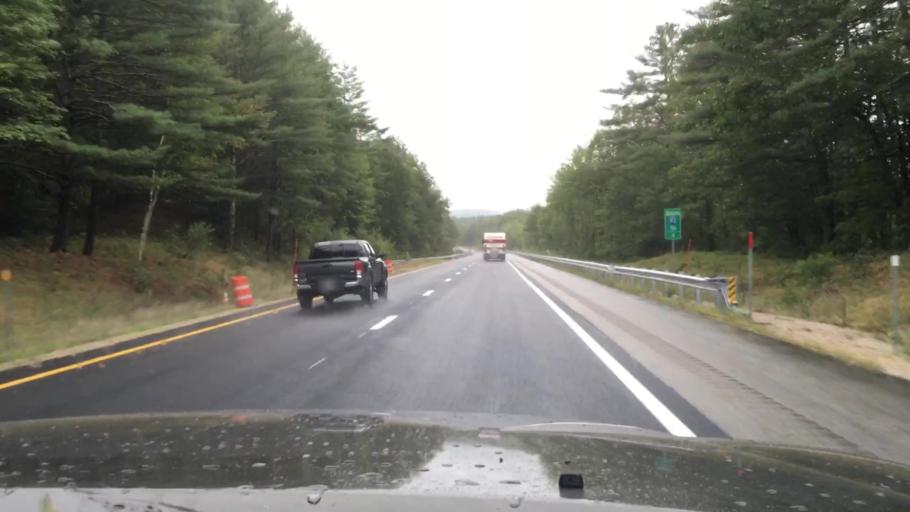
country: US
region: New Hampshire
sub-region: Merrimack County
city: Boscawen
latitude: 43.3665
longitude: -71.6116
